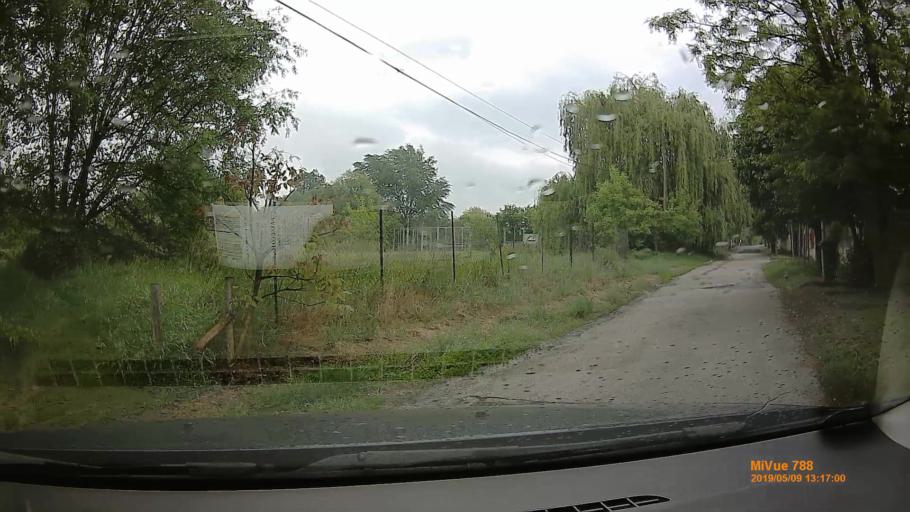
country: HU
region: Budapest
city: Budapest XVI. keruelet
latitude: 47.5417
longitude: 19.1853
